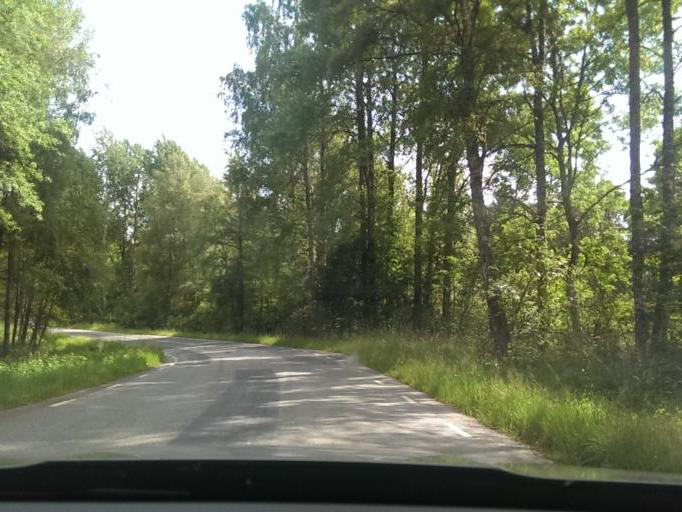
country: SE
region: Joenkoeping
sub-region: Varnamo Kommun
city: Forsheda
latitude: 57.1160
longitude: 13.8748
